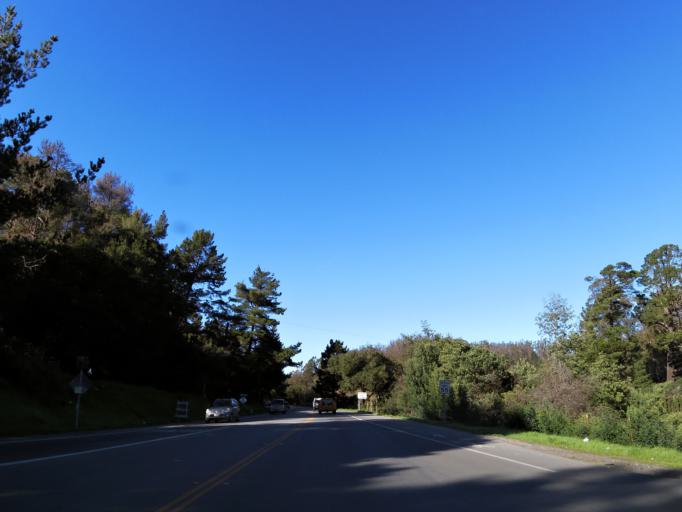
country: US
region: California
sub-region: Monterey County
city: Prunedale
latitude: 36.8045
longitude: -121.6678
